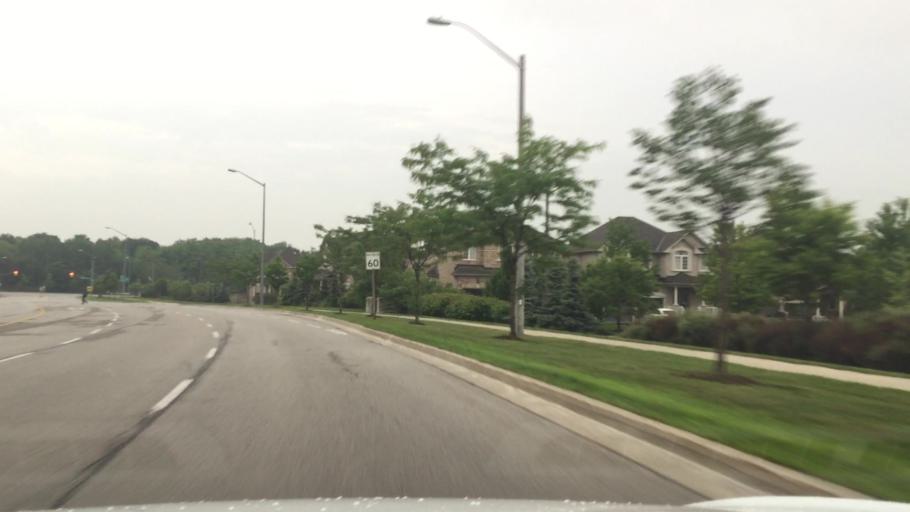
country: CA
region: Ontario
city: Markham
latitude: 43.8586
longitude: -79.2231
